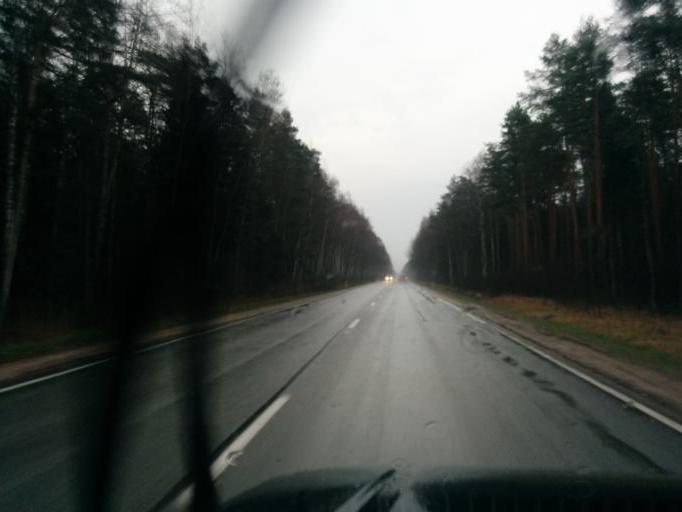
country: LV
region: Kekava
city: Balozi
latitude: 56.8170
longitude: 24.1214
